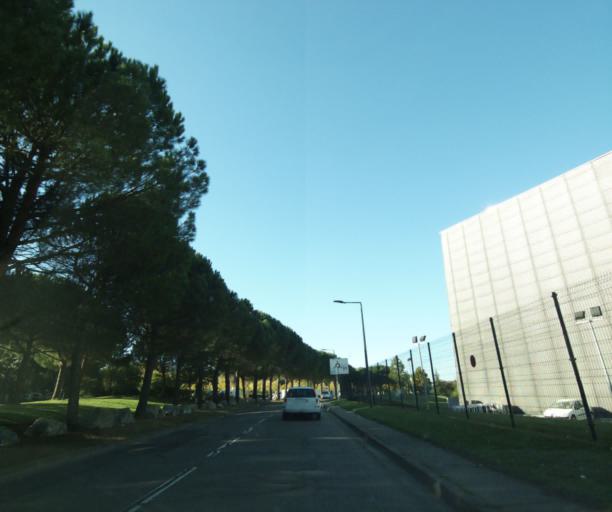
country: FR
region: Midi-Pyrenees
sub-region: Departement de la Haute-Garonne
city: Balma
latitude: 43.5856
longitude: 1.4916
